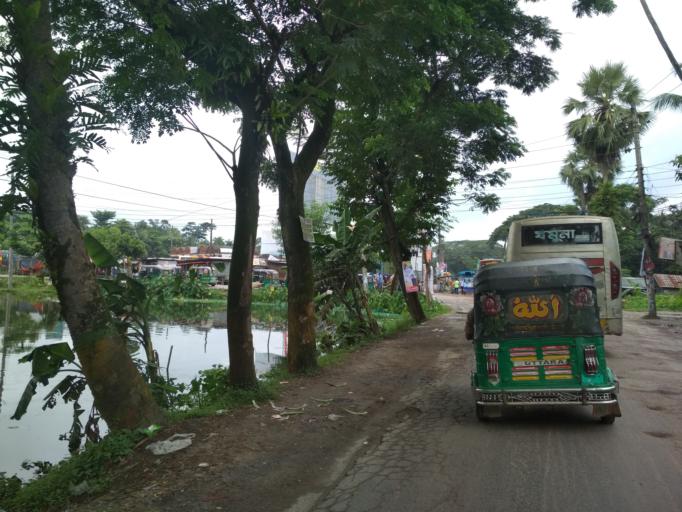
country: BD
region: Chittagong
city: Lakshmipur
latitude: 22.9463
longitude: 90.8143
